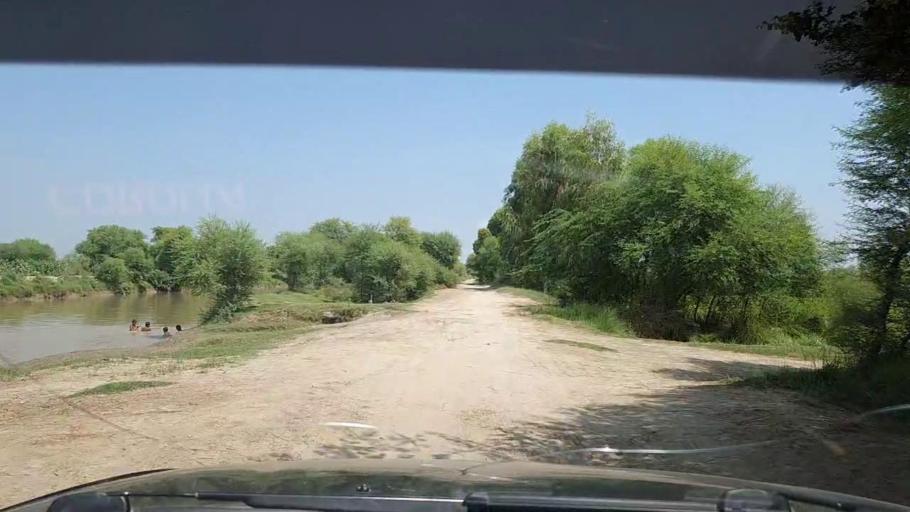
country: PK
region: Sindh
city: Tangwani
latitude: 28.2332
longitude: 68.9700
